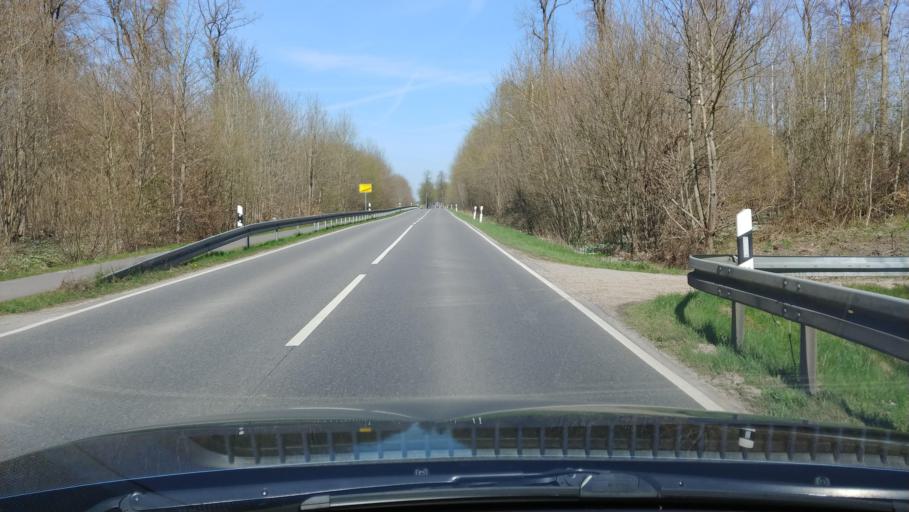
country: DE
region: Mecklenburg-Vorpommern
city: Lubstorf
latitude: 53.7310
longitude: 11.4043
